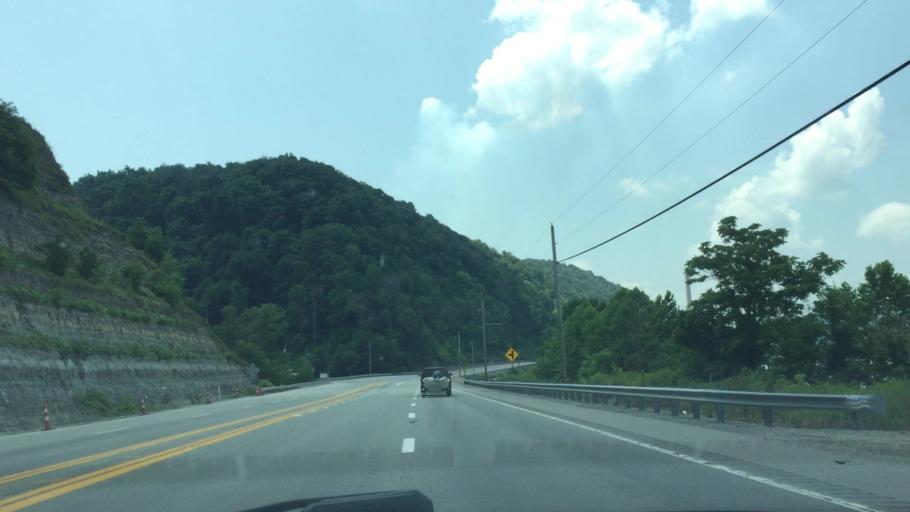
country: US
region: Ohio
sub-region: Belmont County
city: Powhatan Point
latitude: 39.8609
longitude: -80.7918
